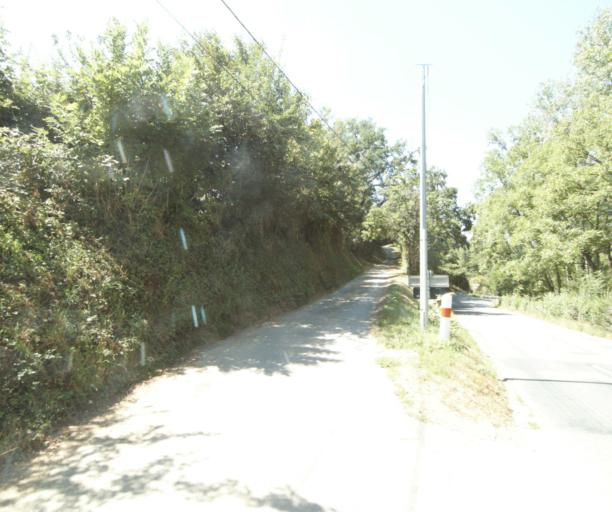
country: FR
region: Rhone-Alpes
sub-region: Departement du Rhone
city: Courzieu
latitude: 45.7470
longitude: 4.5664
